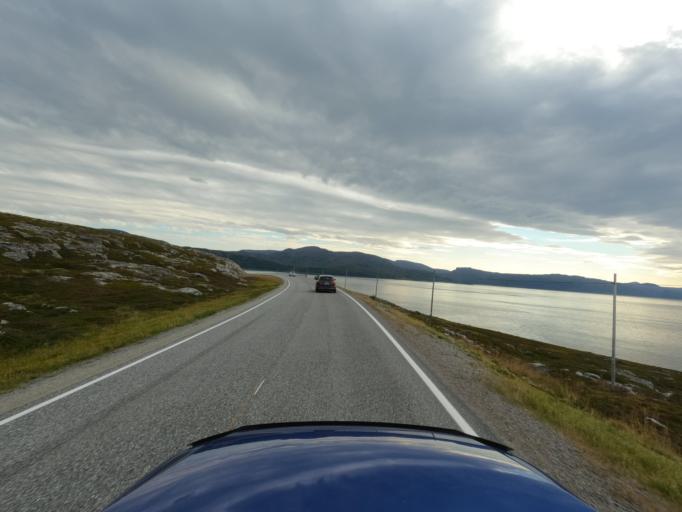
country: NO
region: Finnmark Fylke
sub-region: Hammerfest
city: Rypefjord
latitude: 70.5132
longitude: 23.7733
